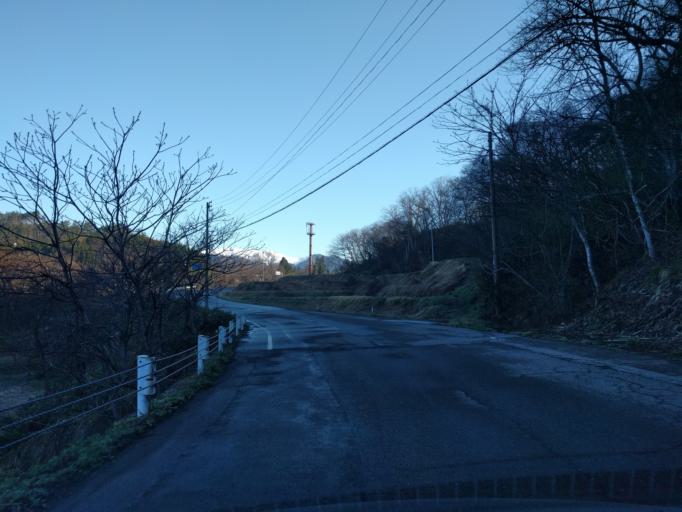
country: JP
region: Fukushima
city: Kitakata
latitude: 37.6913
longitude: 139.7897
